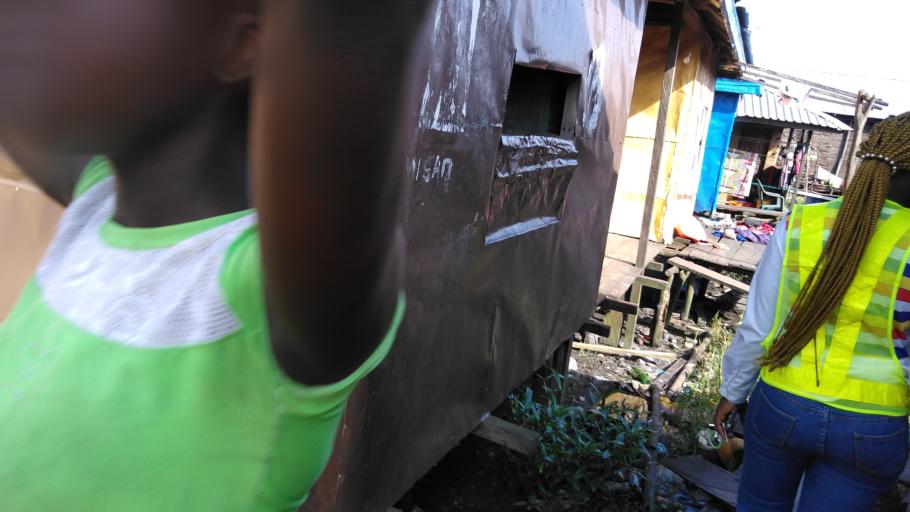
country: NG
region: Ondo
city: Igbekebo
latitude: 5.9220
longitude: 4.9686
